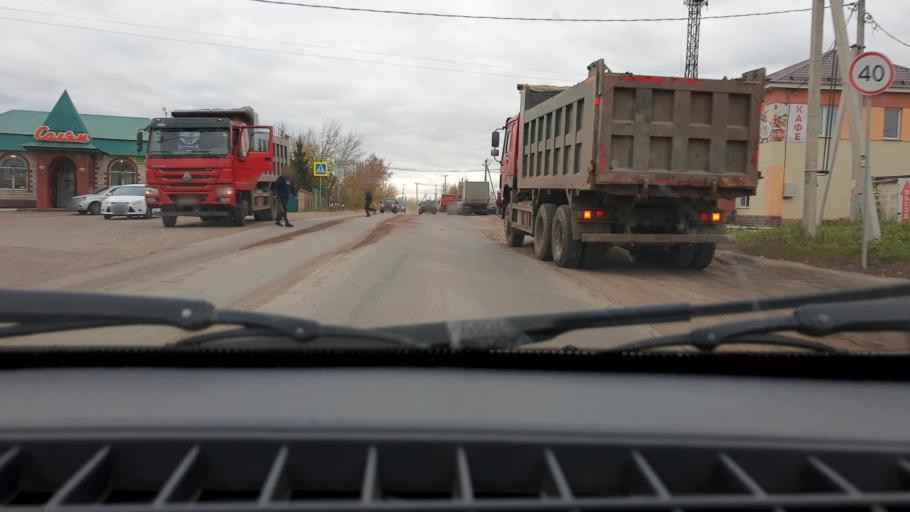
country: RU
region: Bashkortostan
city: Ufa
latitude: 54.5694
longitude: 55.9313
